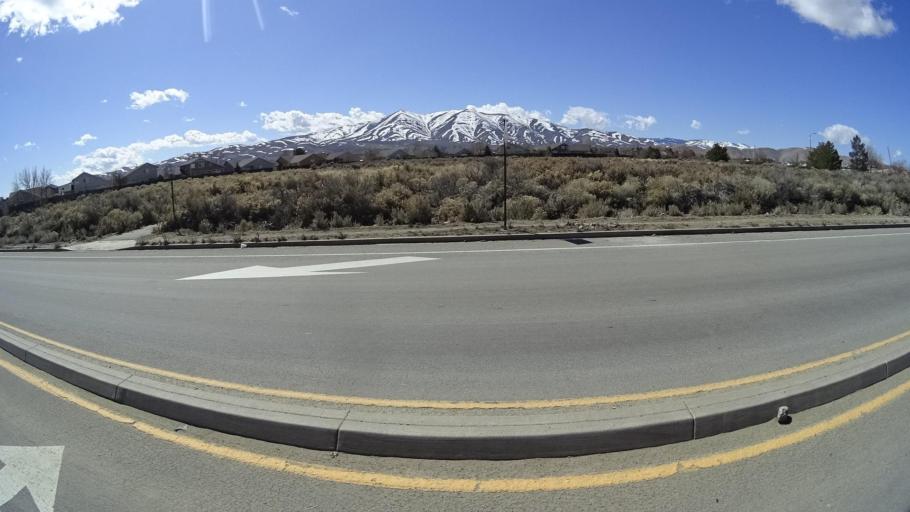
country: US
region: Nevada
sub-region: Washoe County
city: Lemmon Valley
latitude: 39.6432
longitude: -119.8634
